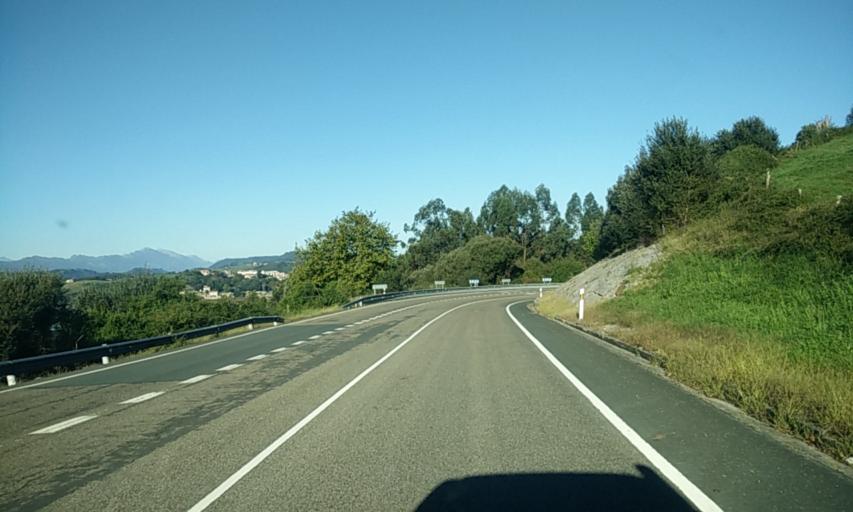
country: ES
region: Cantabria
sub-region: Provincia de Cantabria
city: San Vicente de la Barquera
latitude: 43.3805
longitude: -4.3796
